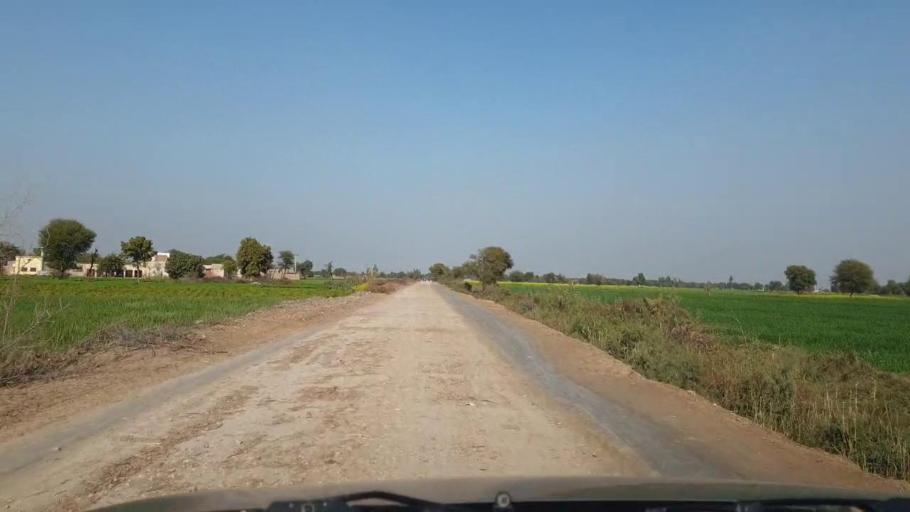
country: PK
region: Sindh
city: Jhol
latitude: 25.9337
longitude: 68.8781
